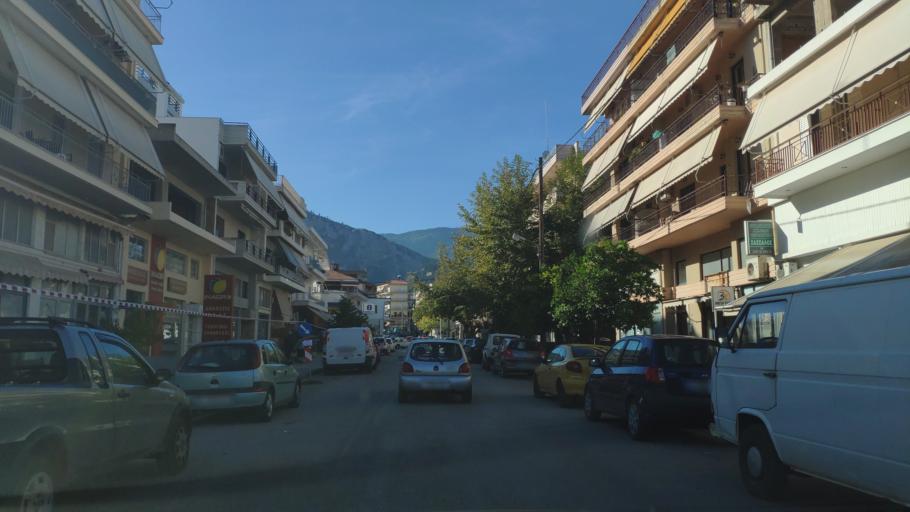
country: GR
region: Central Greece
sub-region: Nomos Voiotias
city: Livadeia
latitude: 38.4423
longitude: 22.8783
